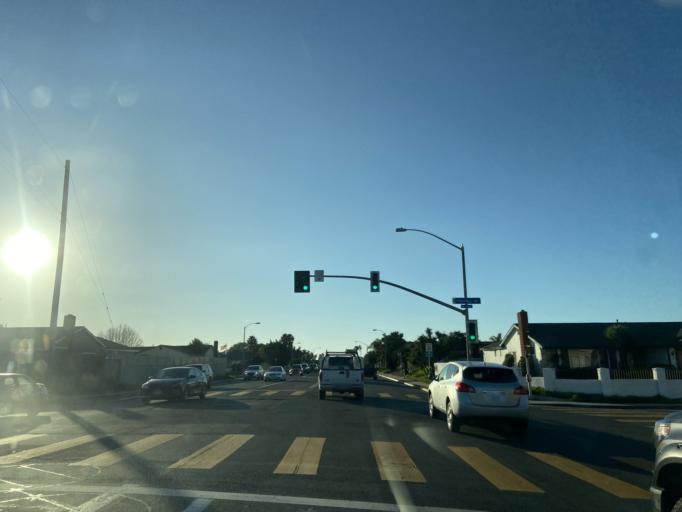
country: US
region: California
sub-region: San Diego County
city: Imperial Beach
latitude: 32.5766
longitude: -117.0969
